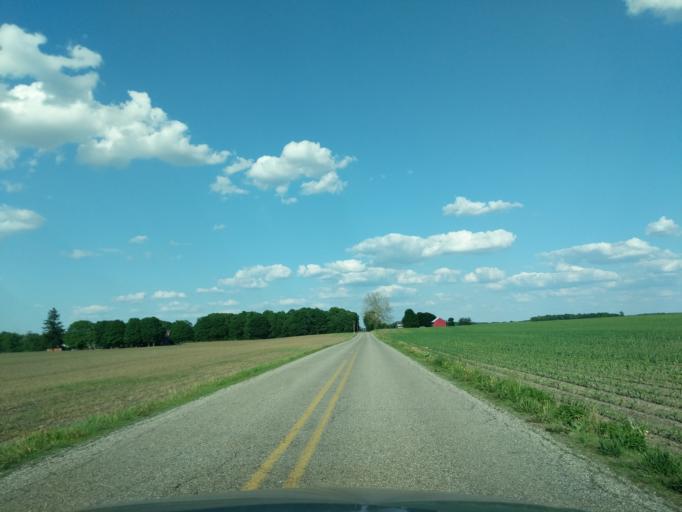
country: US
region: Indiana
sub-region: Kosciusko County
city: North Webster
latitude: 41.3024
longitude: -85.6276
